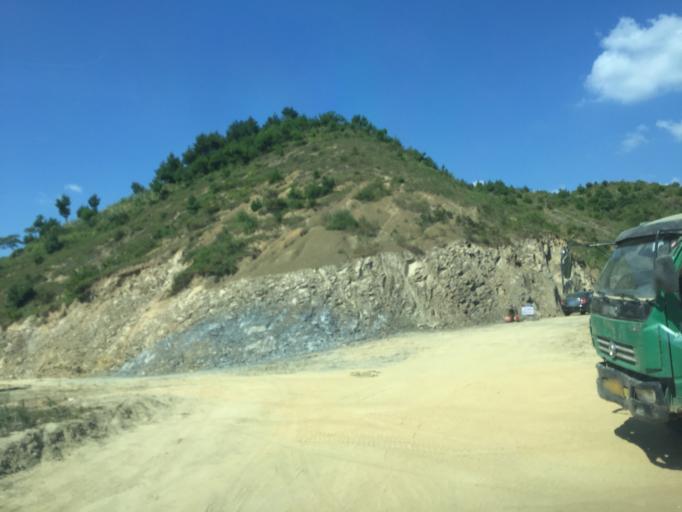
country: CN
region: Guizhou Sheng
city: Tongjing
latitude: 28.3304
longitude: 108.2939
